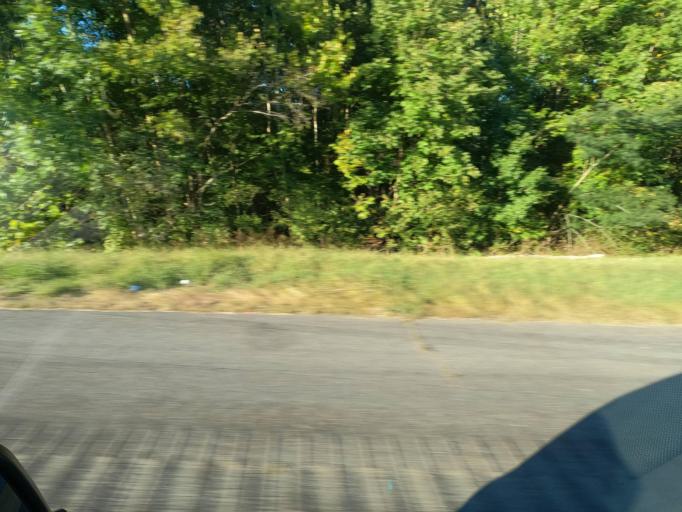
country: US
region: Tennessee
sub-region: Shelby County
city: Arlington
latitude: 35.3117
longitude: -89.7142
